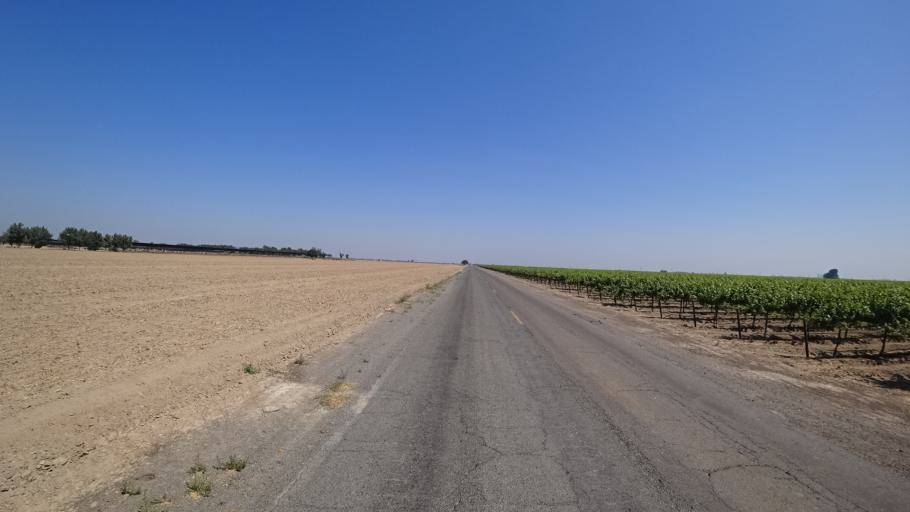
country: US
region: California
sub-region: Fresno County
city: Kingsburg
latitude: 36.4100
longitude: -119.5288
